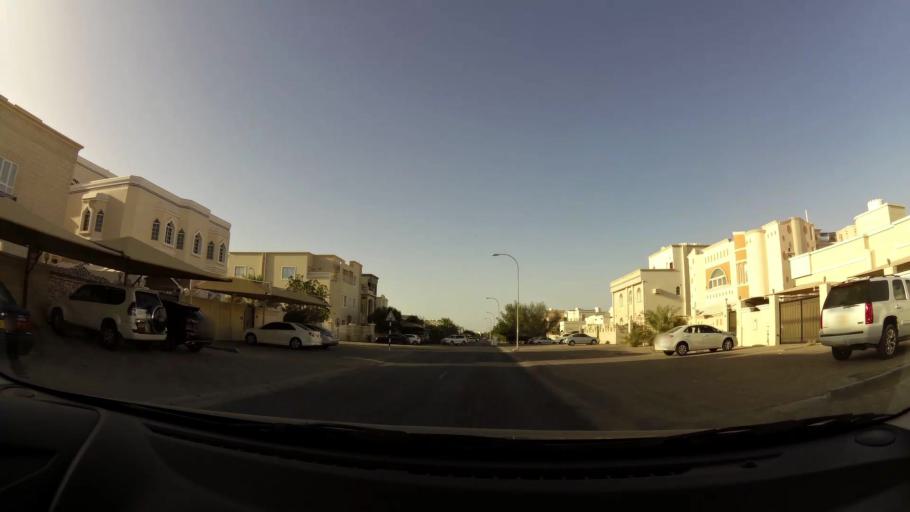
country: OM
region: Muhafazat Masqat
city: As Sib al Jadidah
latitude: 23.6086
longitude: 58.2189
